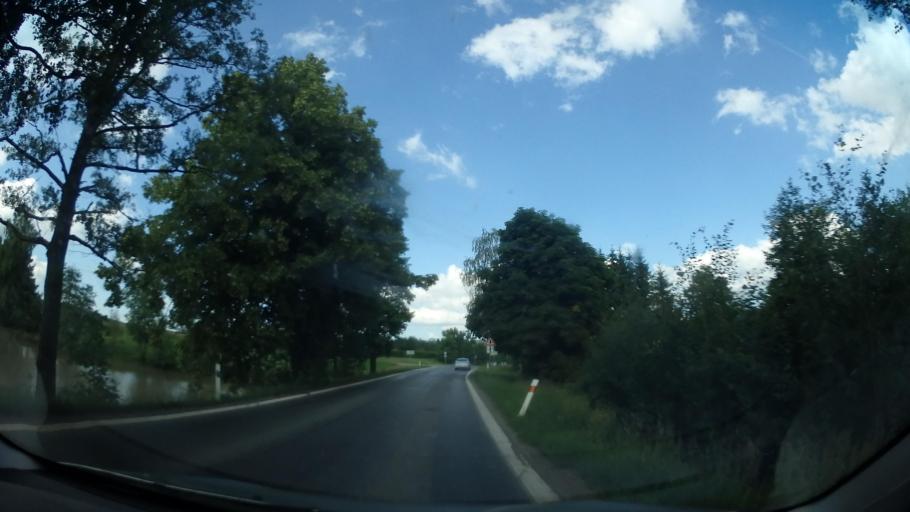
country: CZ
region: Vysocina
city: Zd'ar nad Sazavou Druhy
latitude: 49.6179
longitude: 15.9485
